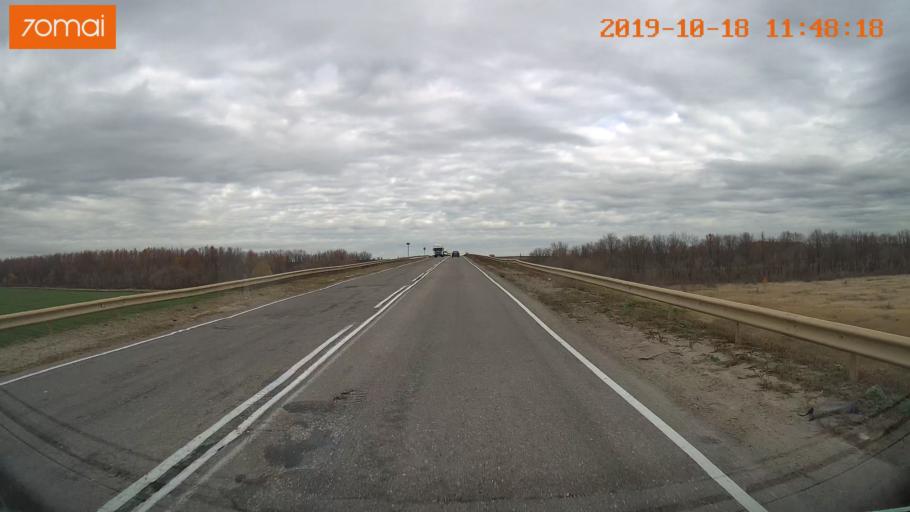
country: RU
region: Rjazan
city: Mikhaylov
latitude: 54.2383
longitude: 38.9822
